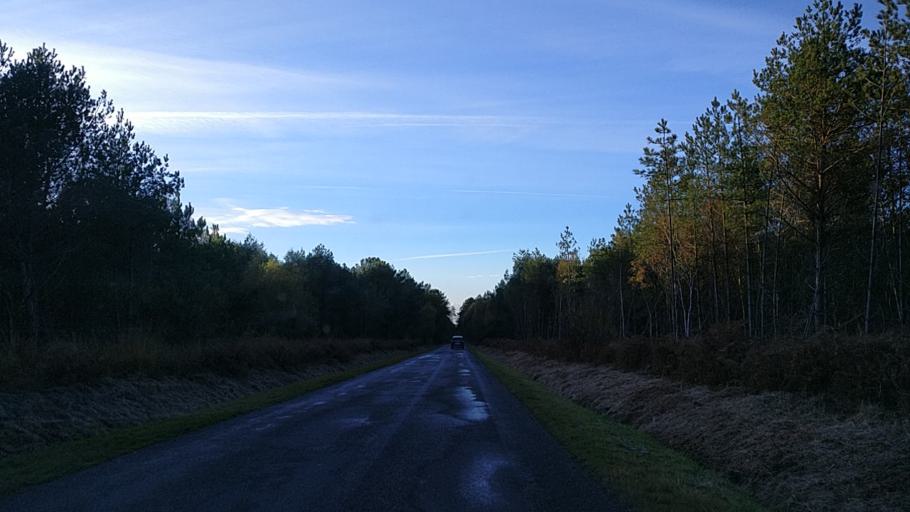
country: FR
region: Brittany
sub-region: Departement d'Ille-et-Vilaine
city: Saint-Sulpice-la-Foret
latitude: 48.1898
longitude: -1.5510
